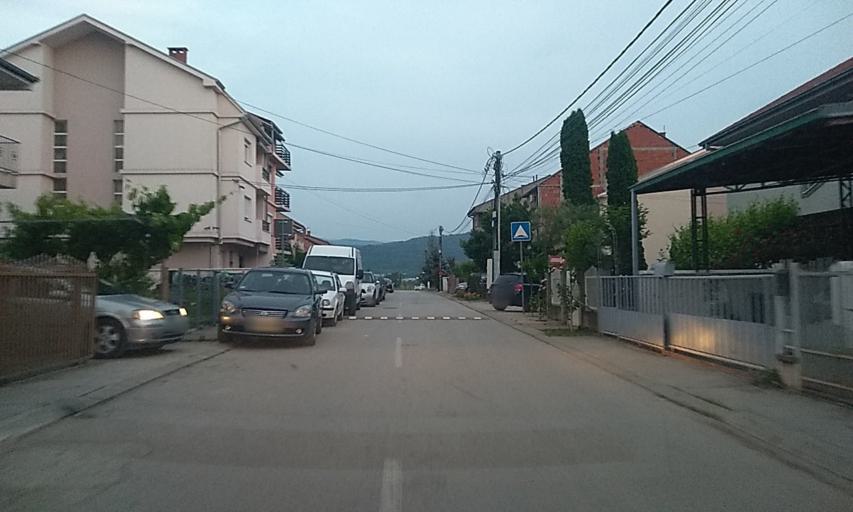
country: RS
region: Central Serbia
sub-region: Nisavski Okrug
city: Nis
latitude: 43.3236
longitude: 21.9457
